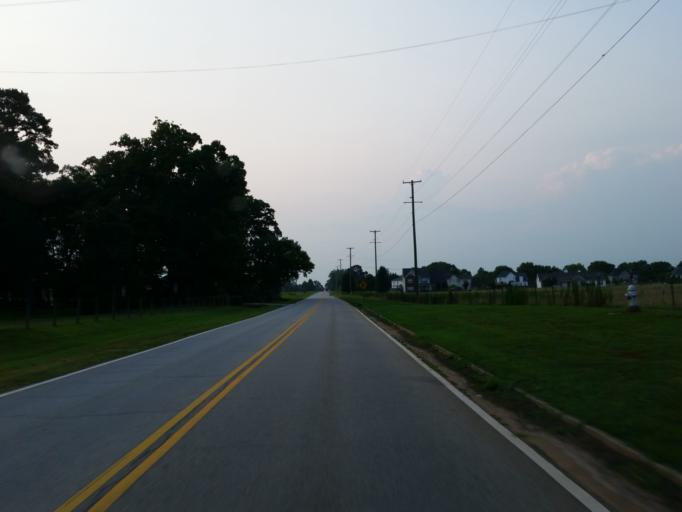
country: US
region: Georgia
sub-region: Henry County
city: Hampton
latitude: 33.3954
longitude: -84.2125
